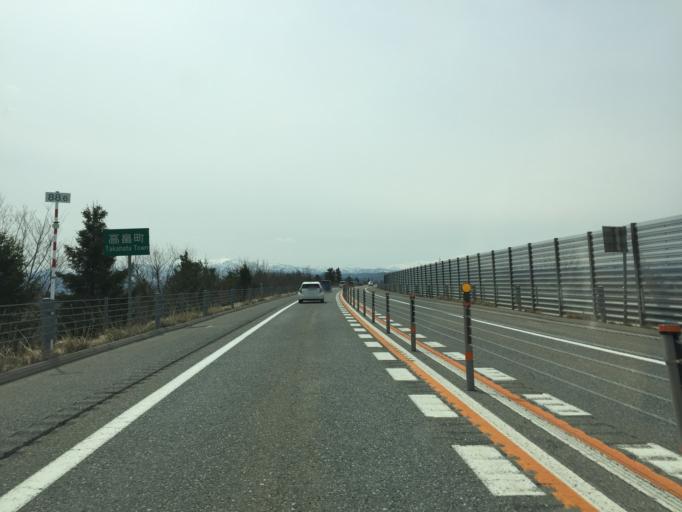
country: JP
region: Yamagata
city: Takahata
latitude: 37.9730
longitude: 140.1363
